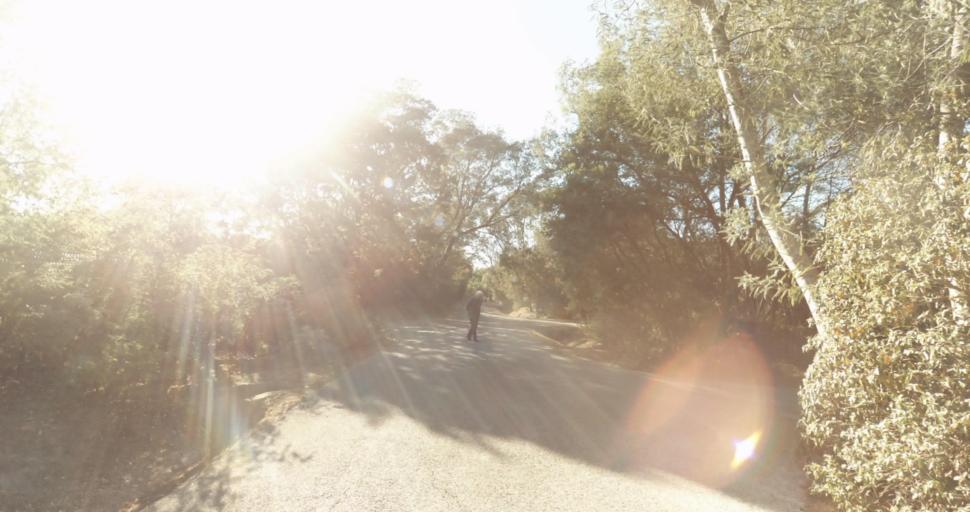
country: FR
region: Provence-Alpes-Cote d'Azur
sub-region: Departement du Var
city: Gassin
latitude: 43.2348
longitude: 6.6000
